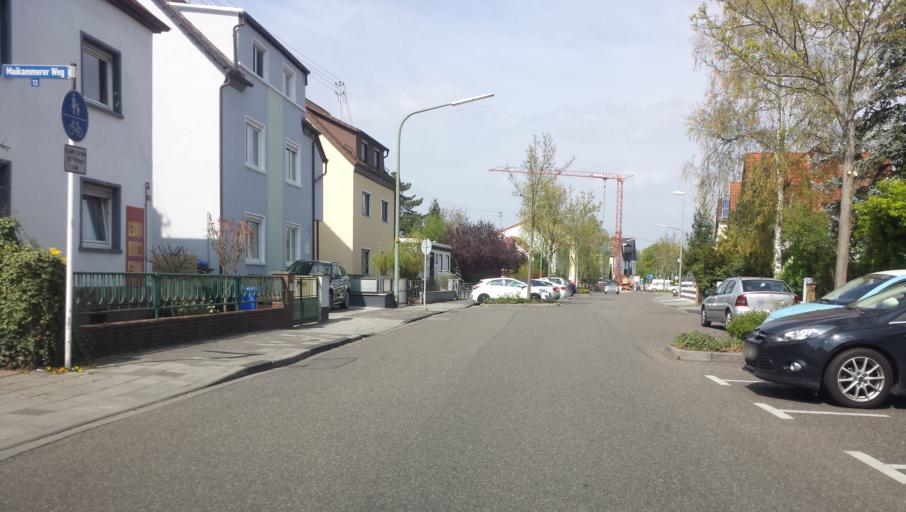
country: DE
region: Rheinland-Pfalz
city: Gartenstadt
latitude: 49.4550
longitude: 8.4004
